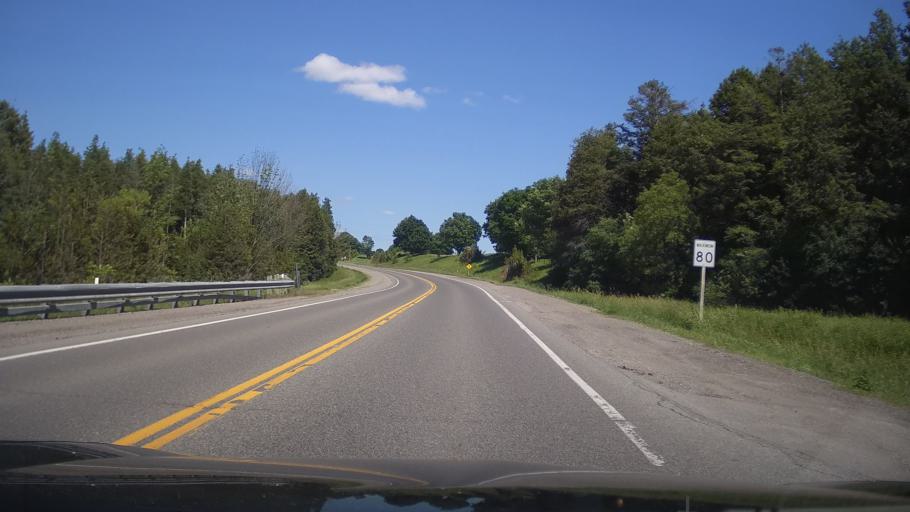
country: CA
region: Ontario
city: Oshawa
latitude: 43.9729
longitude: -78.8795
